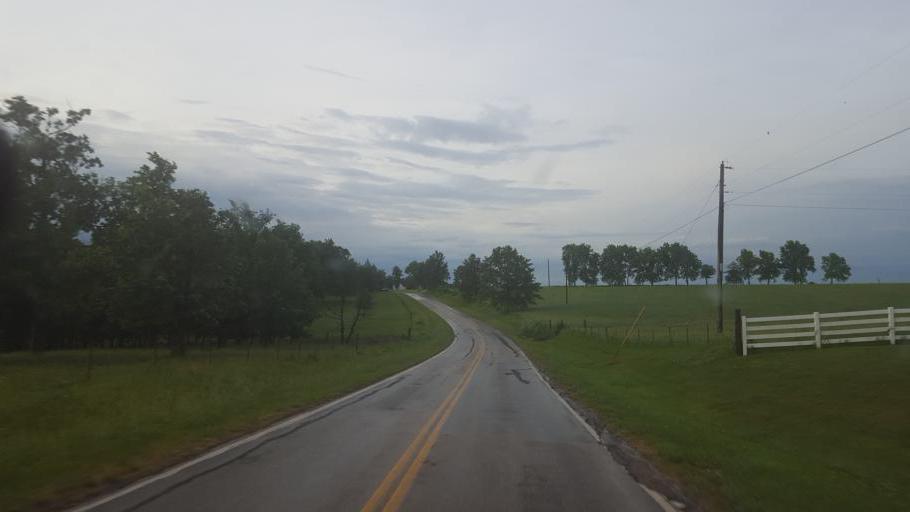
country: US
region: Missouri
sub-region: Moniteau County
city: California
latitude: 38.6666
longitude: -92.5843
